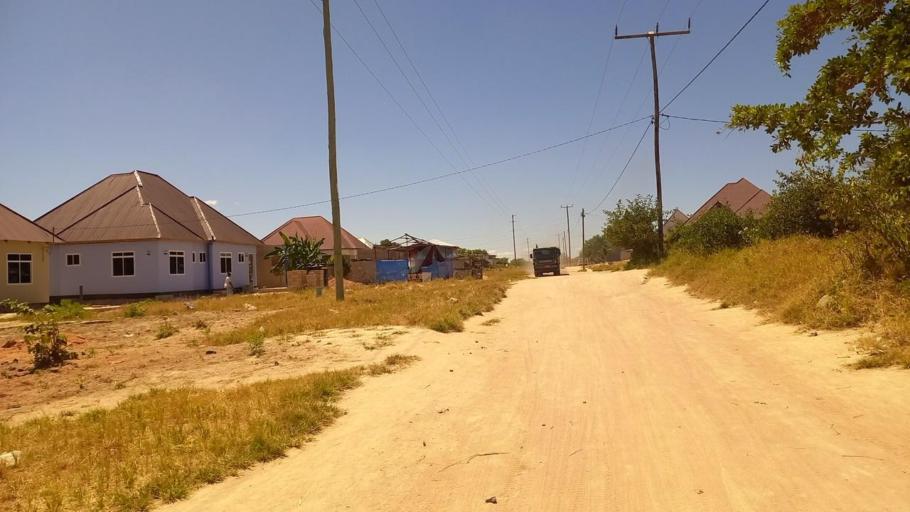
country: TZ
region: Dodoma
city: Dodoma
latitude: -6.1316
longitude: 35.7228
